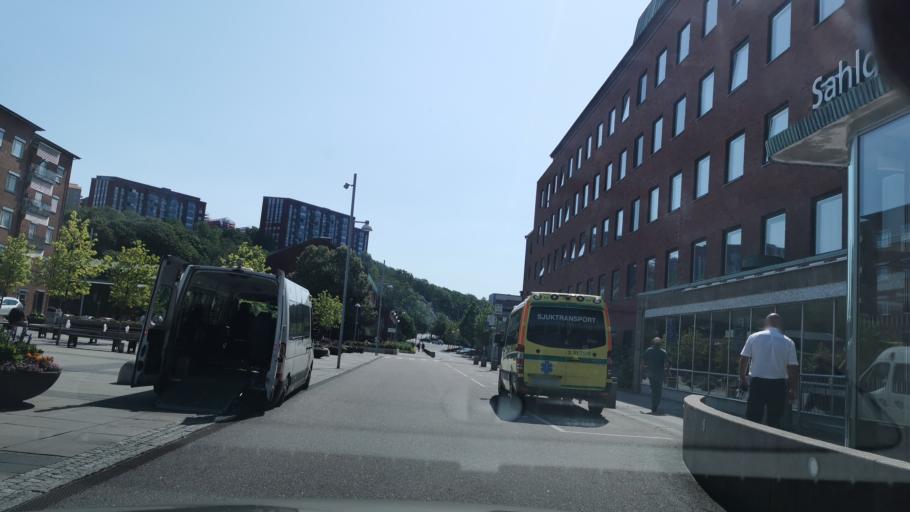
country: SE
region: Vaestra Goetaland
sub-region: Goteborg
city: Goeteborg
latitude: 57.6827
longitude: 11.9617
